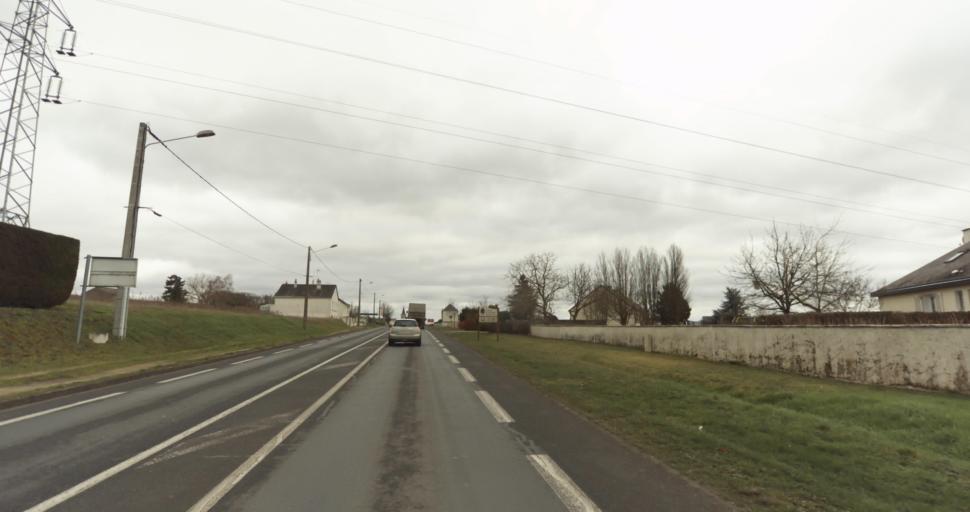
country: FR
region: Pays de la Loire
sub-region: Departement de Maine-et-Loire
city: Varrains
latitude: 47.2310
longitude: -0.0721
